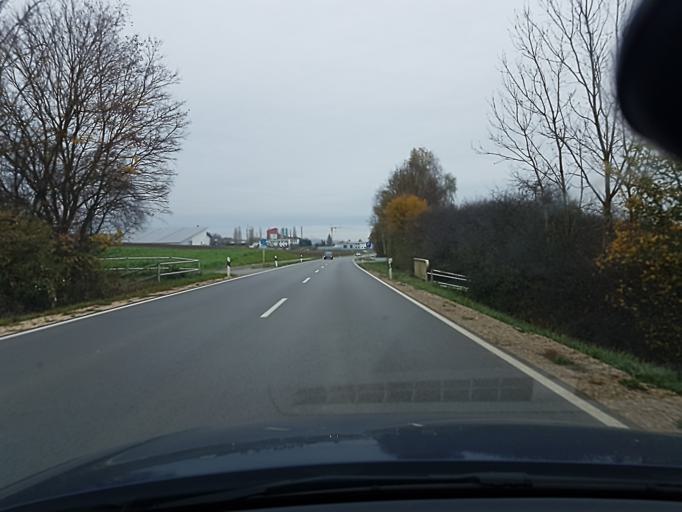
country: DE
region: Bavaria
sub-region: Lower Bavaria
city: Ergoldsbach
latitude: 48.7151
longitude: 12.1915
